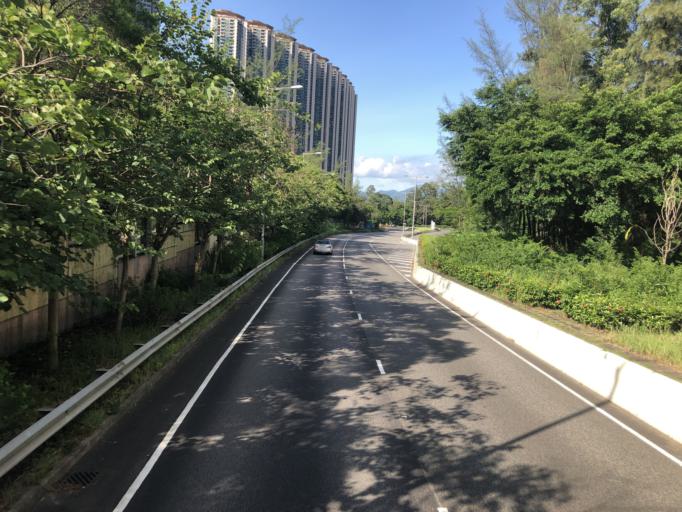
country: HK
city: Tai O
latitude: 22.2874
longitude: 113.9450
